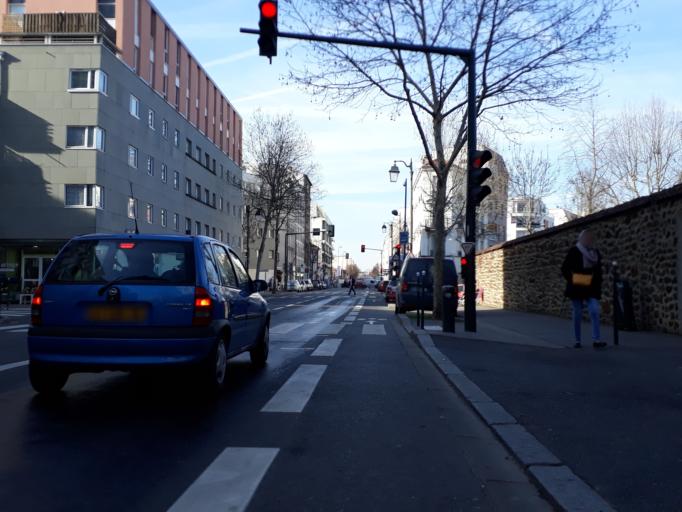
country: FR
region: Ile-de-France
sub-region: Departement des Hauts-de-Seine
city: Asnieres-sur-Seine
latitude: 48.9164
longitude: 2.2900
